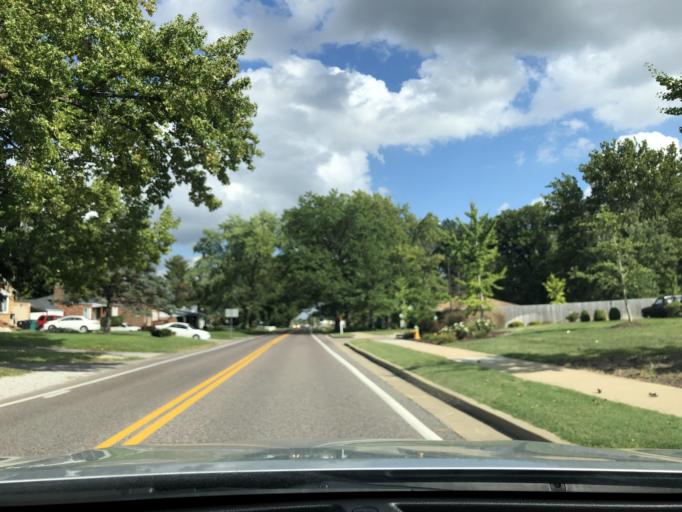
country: US
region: Missouri
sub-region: Saint Louis County
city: Lakeshire
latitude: 38.5440
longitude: -90.3317
